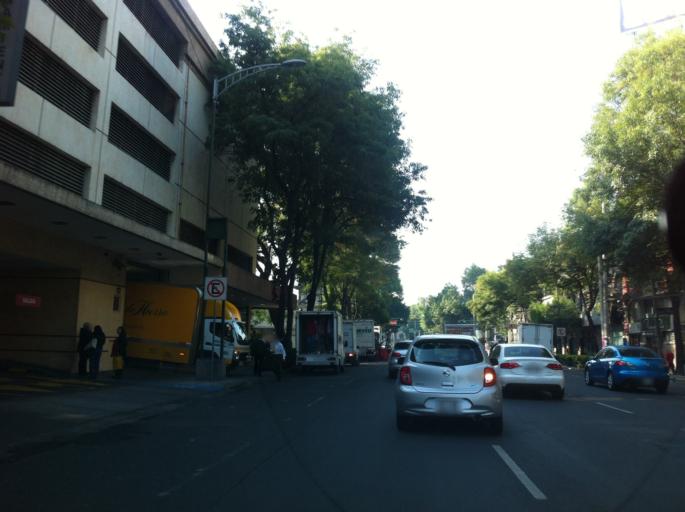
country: MX
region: Mexico City
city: Benito Juarez
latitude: 19.4189
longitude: -99.1694
